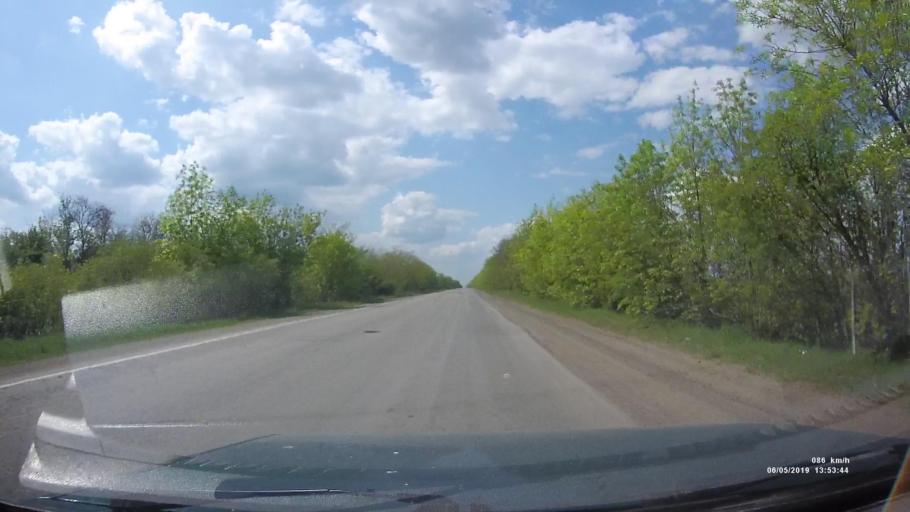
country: RU
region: Rostov
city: Melikhovskaya
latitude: 47.6701
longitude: 40.4578
